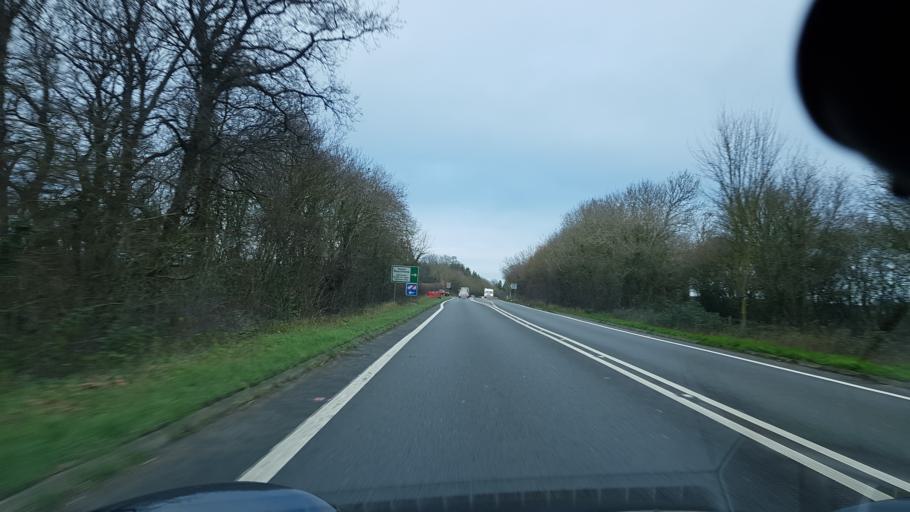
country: GB
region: England
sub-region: Somerset
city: Creech Saint Michael
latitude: 50.9712
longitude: -3.0051
